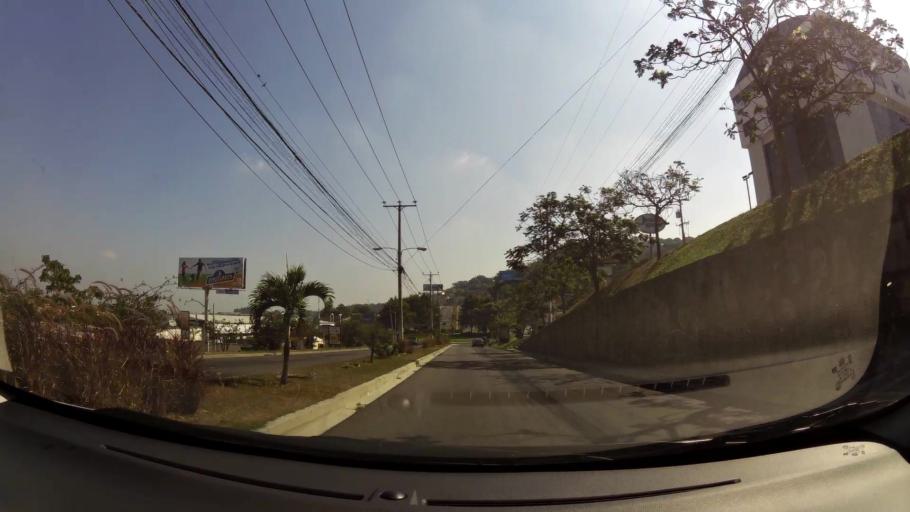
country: SV
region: La Libertad
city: Antiguo Cuscatlan
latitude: 13.6620
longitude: -89.2510
